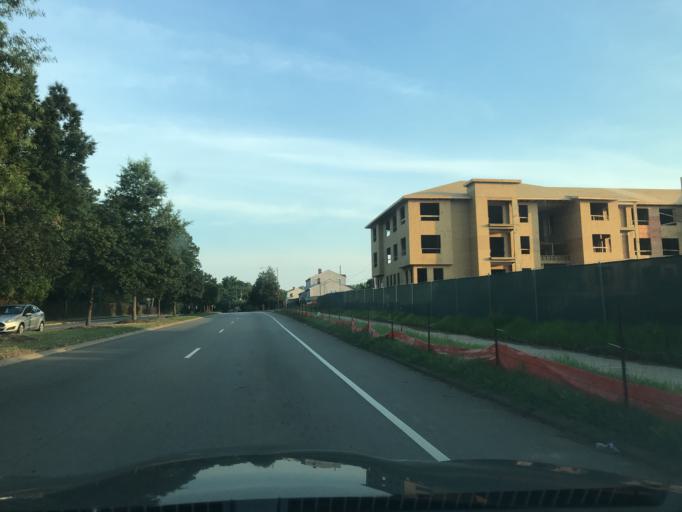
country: US
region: North Carolina
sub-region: Wake County
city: Raleigh
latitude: 35.7867
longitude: -78.6136
